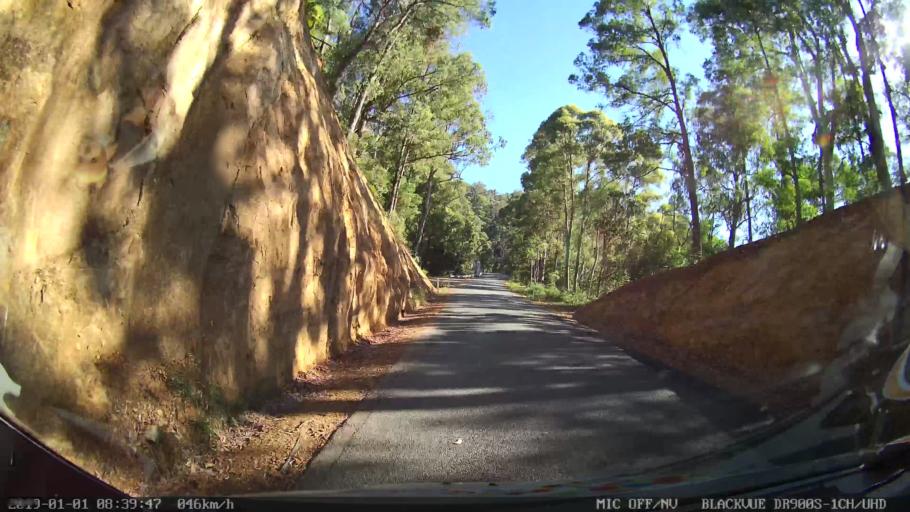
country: AU
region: New South Wales
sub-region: Snowy River
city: Jindabyne
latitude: -36.3290
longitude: 148.1935
